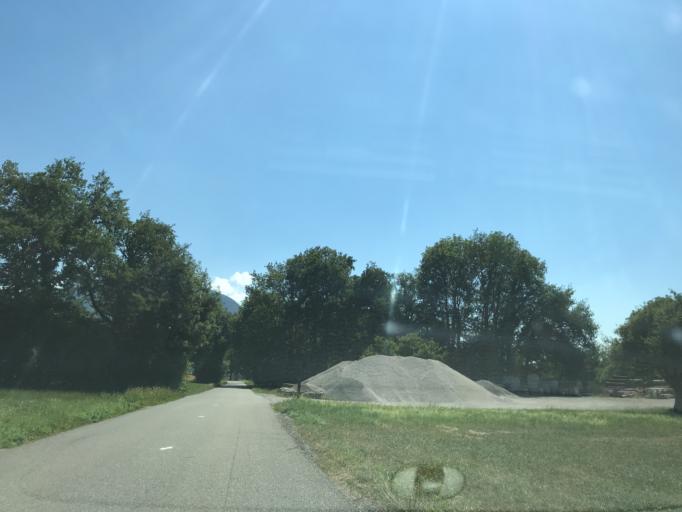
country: FR
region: Rhone-Alpes
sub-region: Departement de la Haute-Savoie
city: Villaz
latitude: 45.9440
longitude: 6.1945
